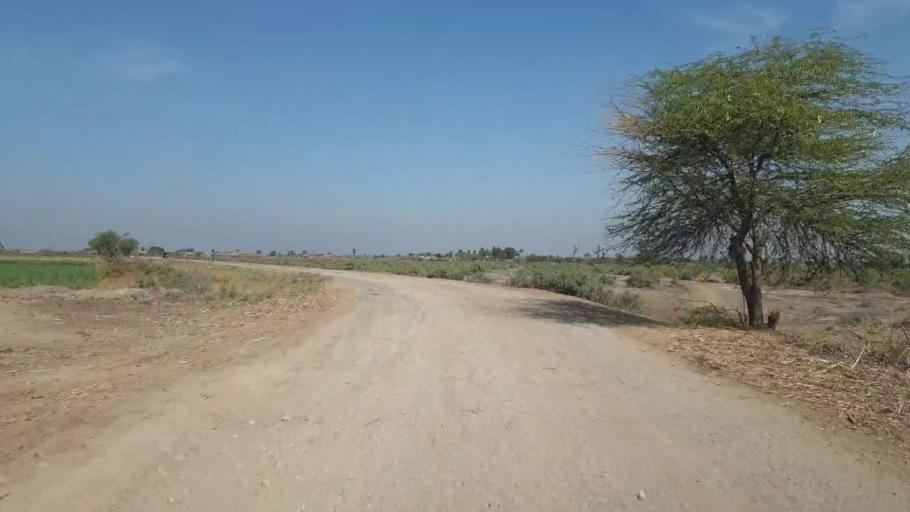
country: PK
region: Sindh
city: Samaro
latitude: 25.3399
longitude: 69.2490
